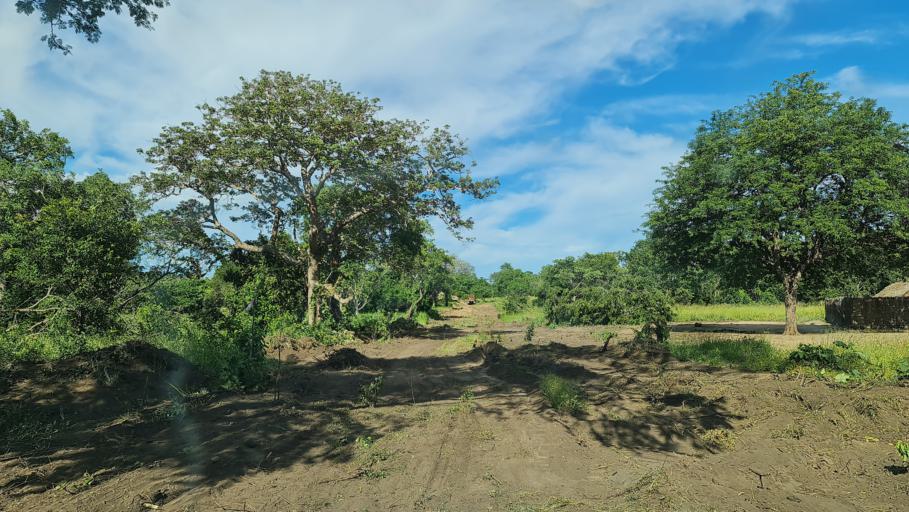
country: MZ
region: Nampula
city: Ilha de Mocambique
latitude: -15.5055
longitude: 40.1502
